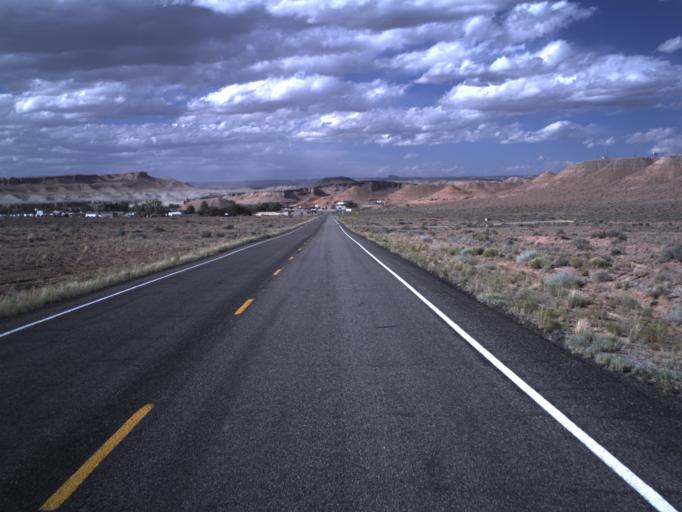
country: US
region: Utah
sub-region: Emery County
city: Ferron
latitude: 38.3633
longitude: -110.7001
